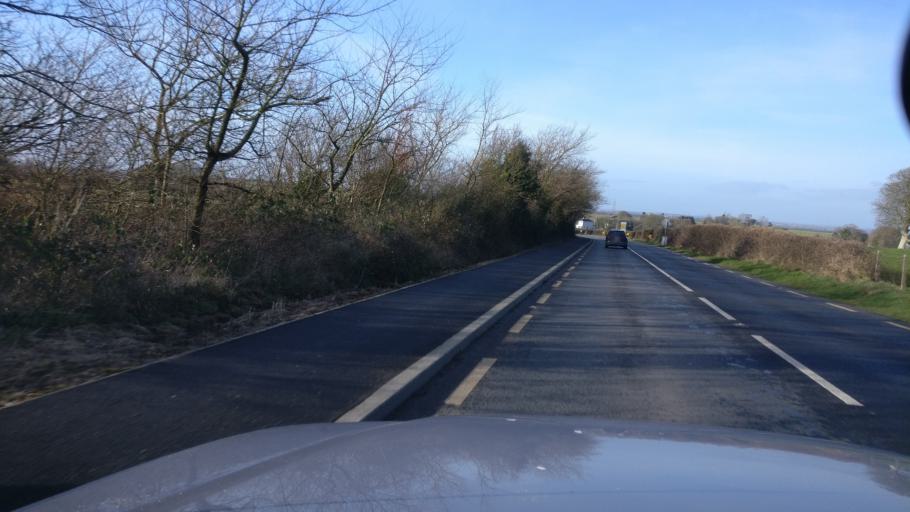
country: IE
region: Leinster
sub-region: Uibh Fhaili
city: Tullamore
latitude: 53.2102
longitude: -7.4396
